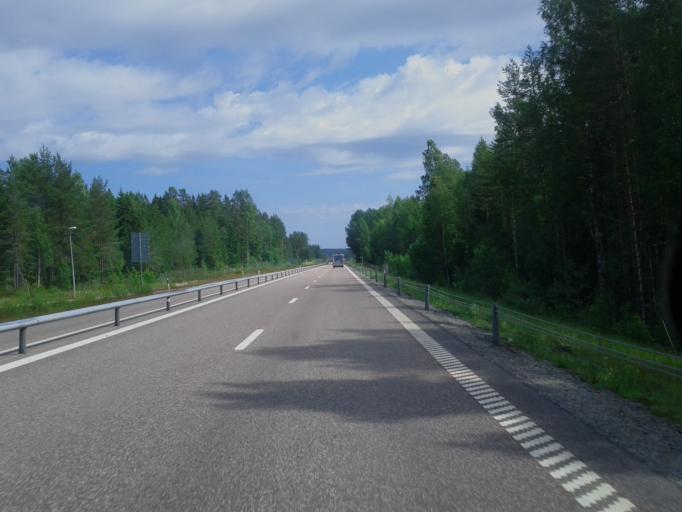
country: SE
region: Vaesternorrland
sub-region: OErnskoeldsviks Kommun
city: Husum
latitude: 63.3178
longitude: 19.0165
